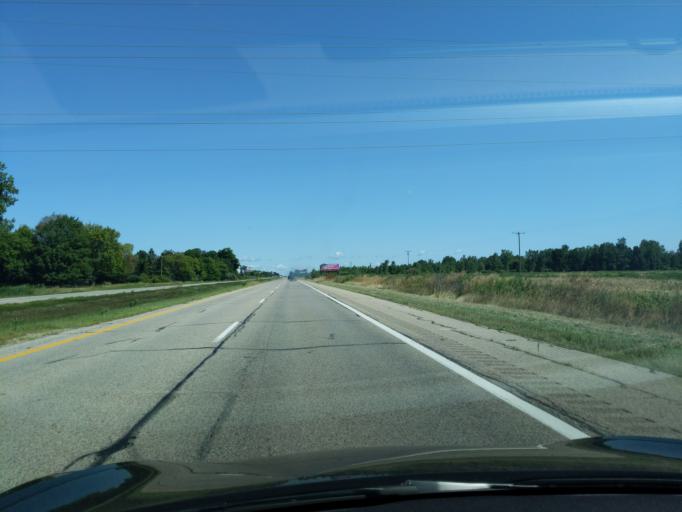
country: US
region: Michigan
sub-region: Gratiot County
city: Ithaca
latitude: 43.2082
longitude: -84.5631
